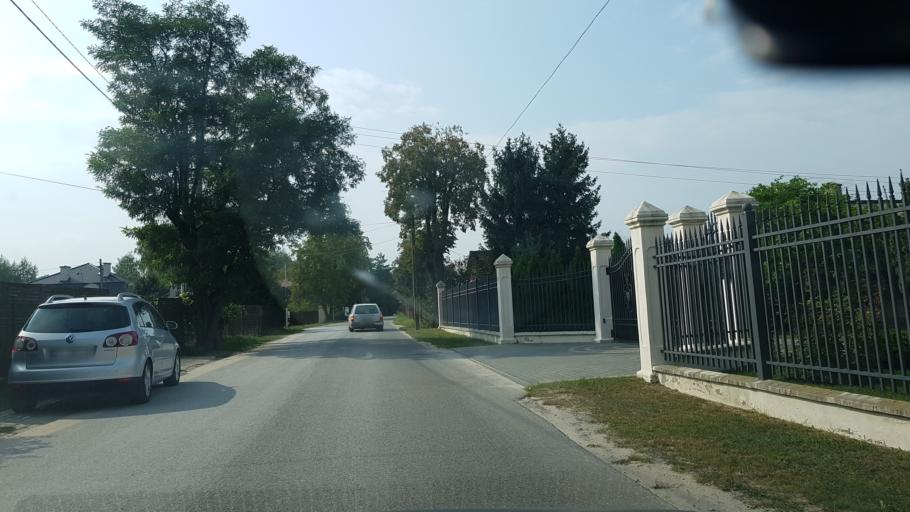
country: PL
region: Masovian Voivodeship
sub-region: Powiat piaseczynski
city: Zabieniec
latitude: 52.0564
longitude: 21.0927
